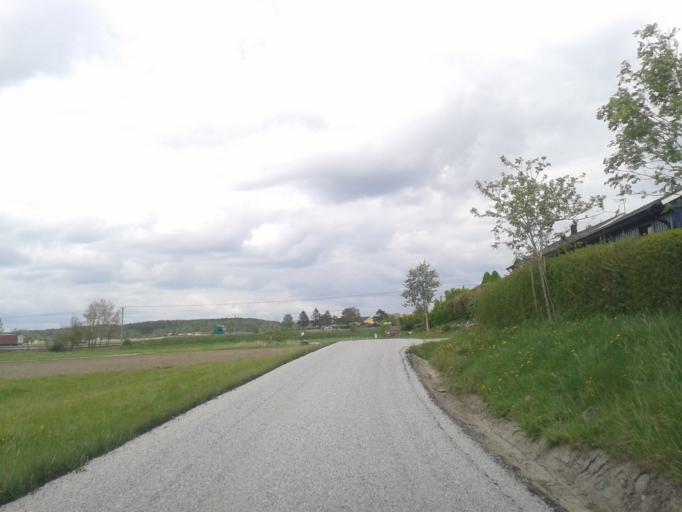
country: SE
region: Vaestra Goetaland
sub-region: Kungalvs Kommun
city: Kungalv
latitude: 57.8984
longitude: 11.9184
